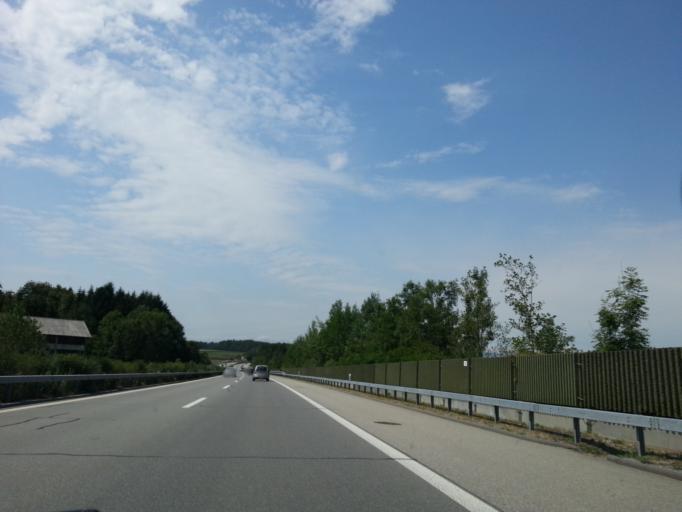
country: CH
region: Bern
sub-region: Bern-Mittelland District
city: Muhleberg
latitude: 46.9606
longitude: 7.2754
